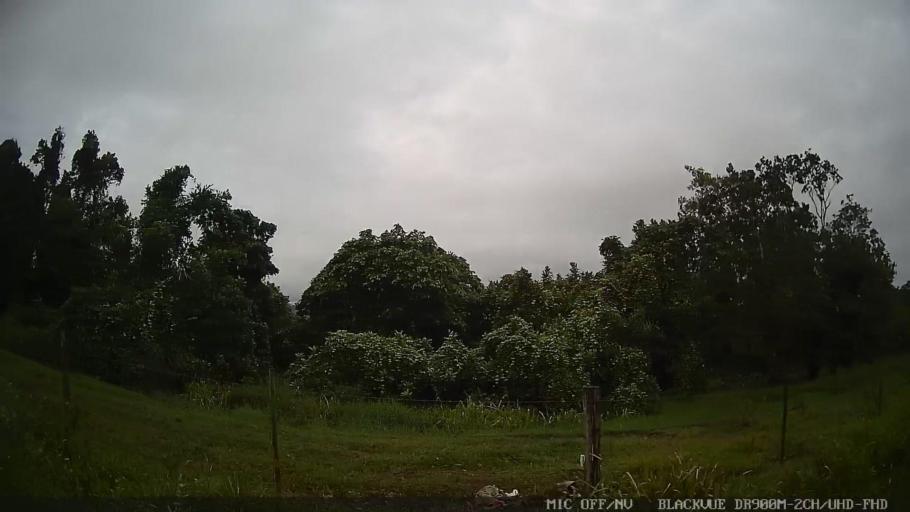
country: BR
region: Sao Paulo
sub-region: Sao Sebastiao
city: Sao Sebastiao
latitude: -23.7096
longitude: -45.4611
